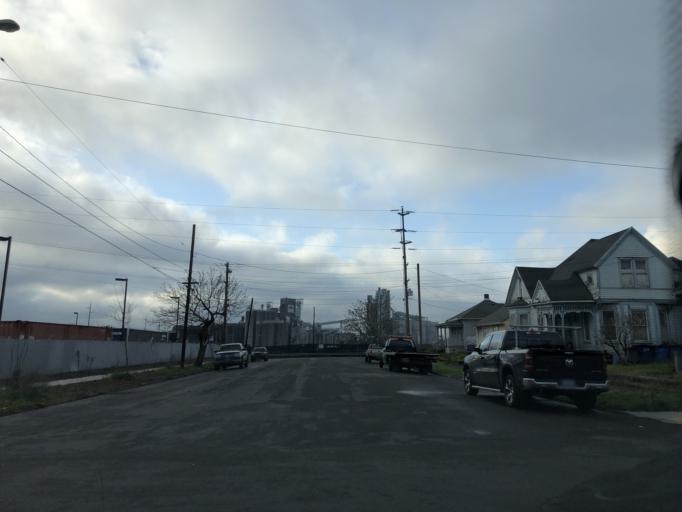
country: US
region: Washington
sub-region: Clark County
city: Vancouver
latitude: 45.6302
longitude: -122.6825
